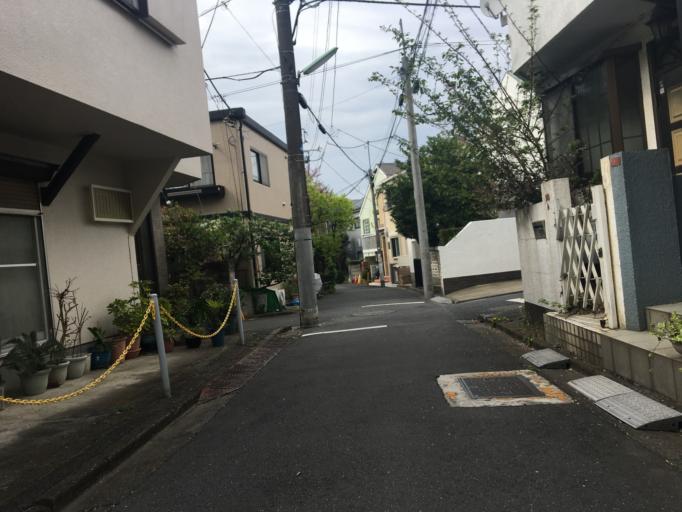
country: JP
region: Tokyo
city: Tokyo
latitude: 35.6988
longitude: 139.6403
